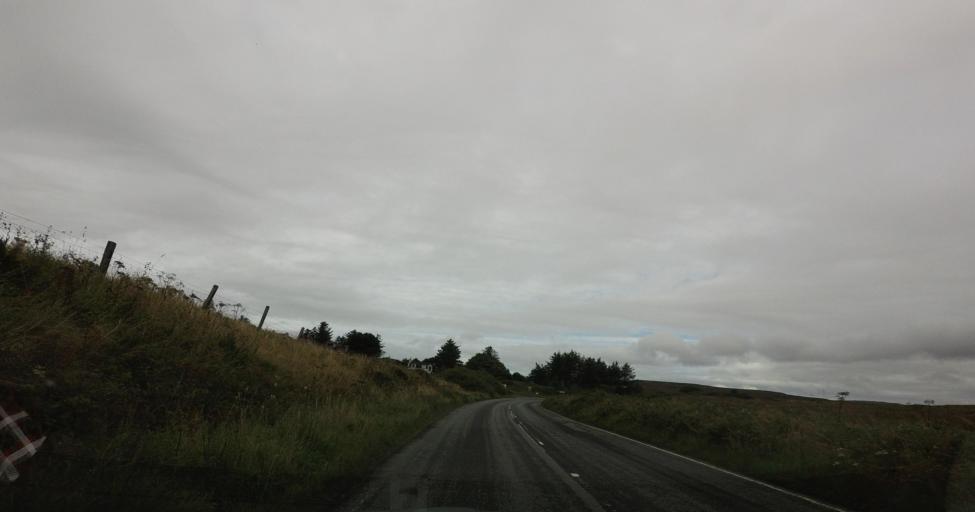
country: GB
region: Scotland
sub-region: Highland
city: Isle of Skye
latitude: 57.4134
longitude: -6.5294
